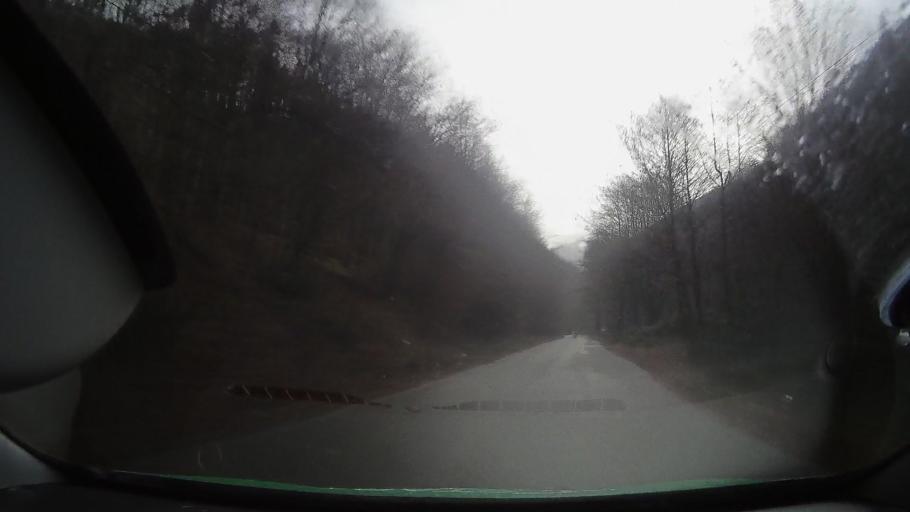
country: RO
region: Hunedoara
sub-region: Comuna Ribita
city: Ribita
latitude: 46.2842
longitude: 22.7365
